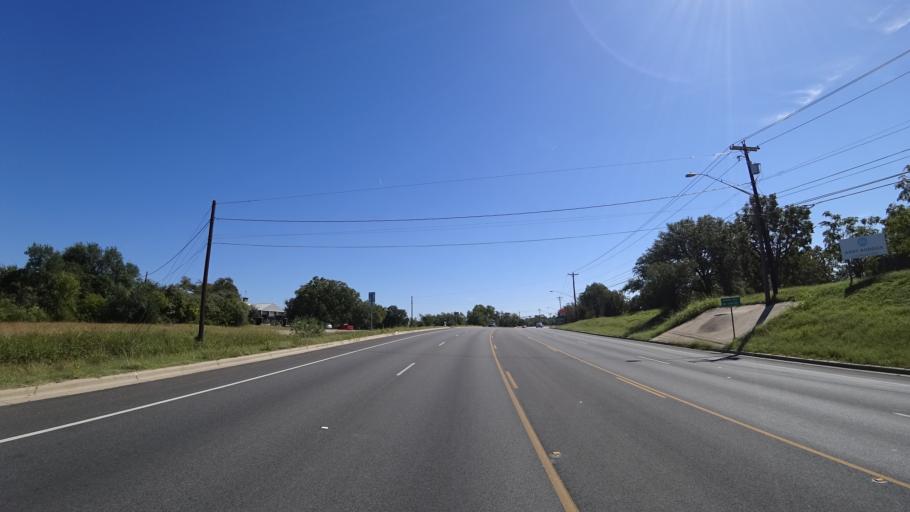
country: US
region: Texas
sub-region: Travis County
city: Hornsby Bend
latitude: 30.2779
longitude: -97.6394
